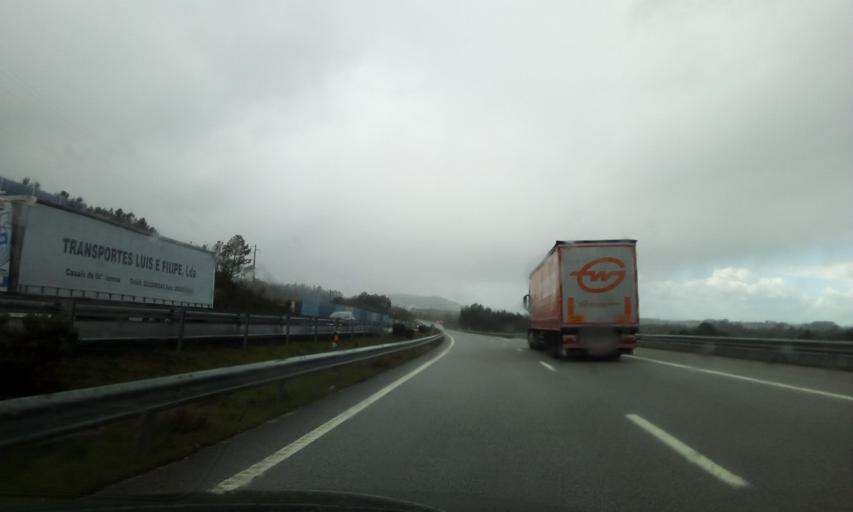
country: PT
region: Viseu
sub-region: Mangualde
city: Mangualde
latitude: 40.6138
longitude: -7.6739
